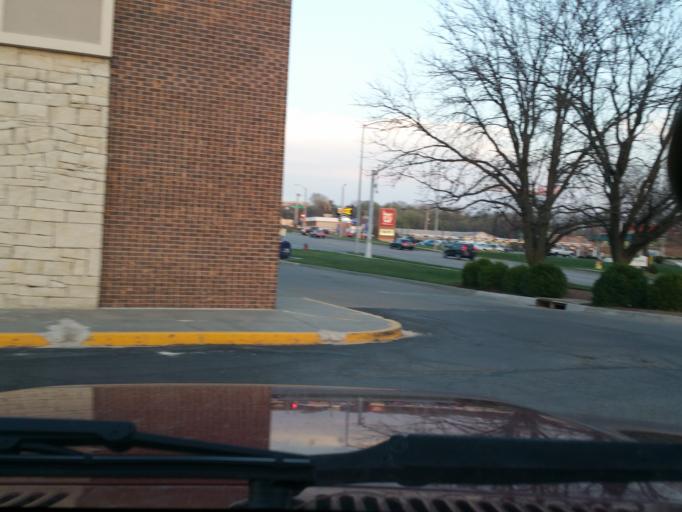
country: US
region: Kansas
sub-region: Riley County
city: Manhattan
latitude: 39.1905
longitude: -96.6084
